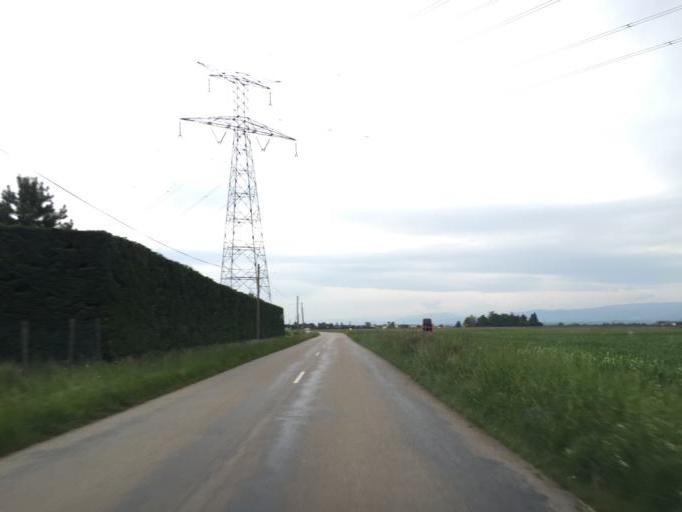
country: FR
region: Rhone-Alpes
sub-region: Departement de la Drome
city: Montelier
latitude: 44.9170
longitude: 5.0444
